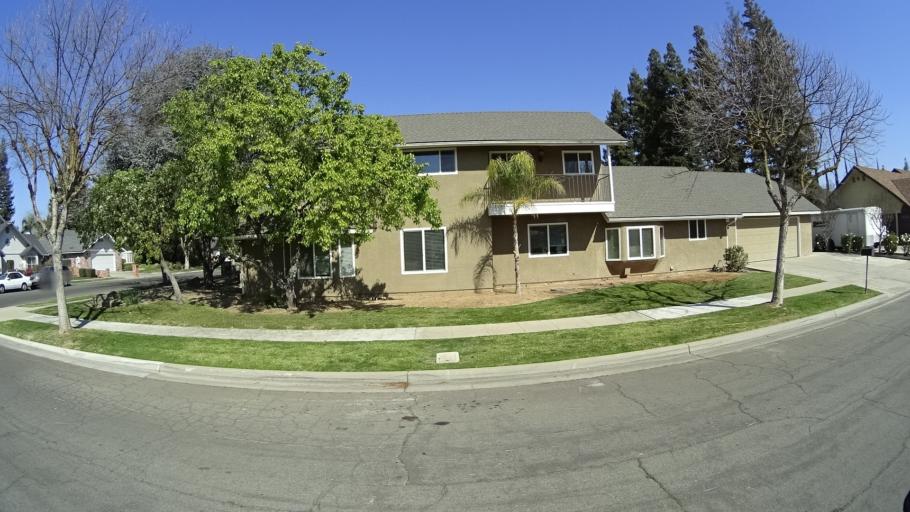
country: US
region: California
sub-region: Fresno County
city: Fresno
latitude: 36.8431
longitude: -119.8214
